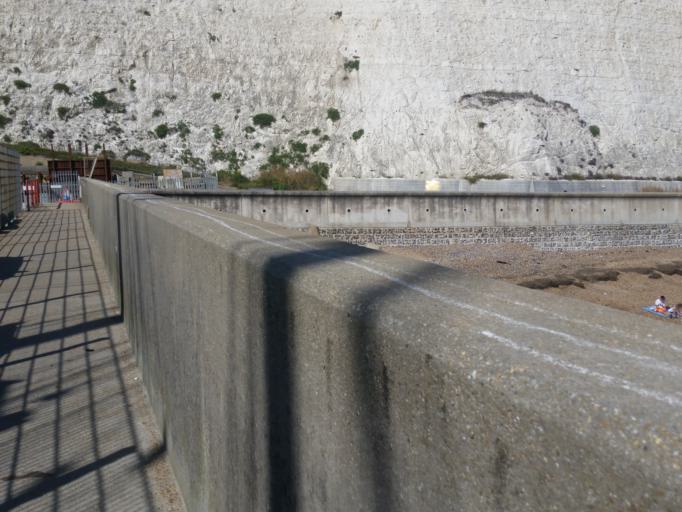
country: GB
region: England
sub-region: Brighton and Hove
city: Rottingdean
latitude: 50.8117
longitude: -0.0927
